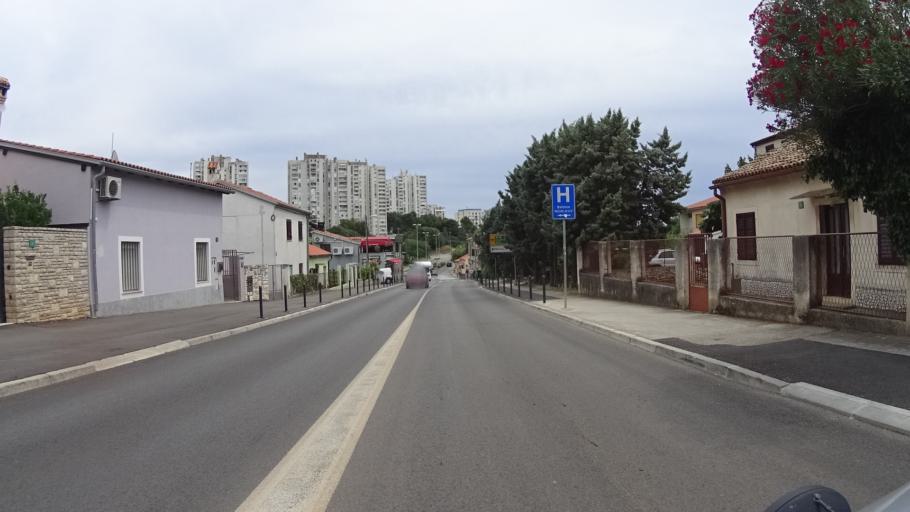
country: HR
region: Istarska
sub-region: Grad Pula
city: Pula
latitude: 44.8554
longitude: 13.8370
